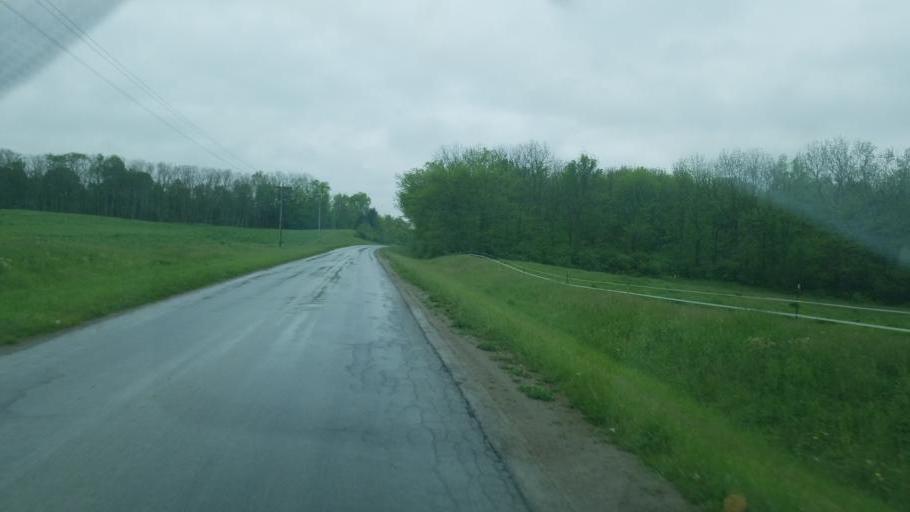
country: US
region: Ohio
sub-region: Highland County
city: Greenfield
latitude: 39.2877
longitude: -83.4585
